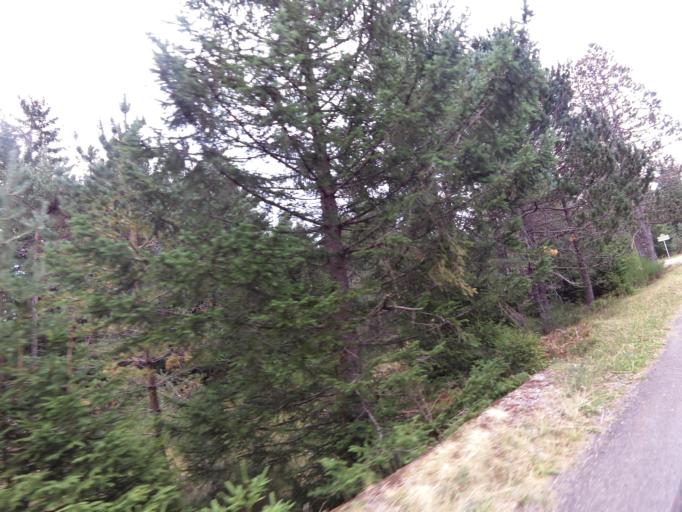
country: FR
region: Languedoc-Roussillon
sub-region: Departement du Gard
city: Valleraugue
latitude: 44.0837
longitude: 3.5631
